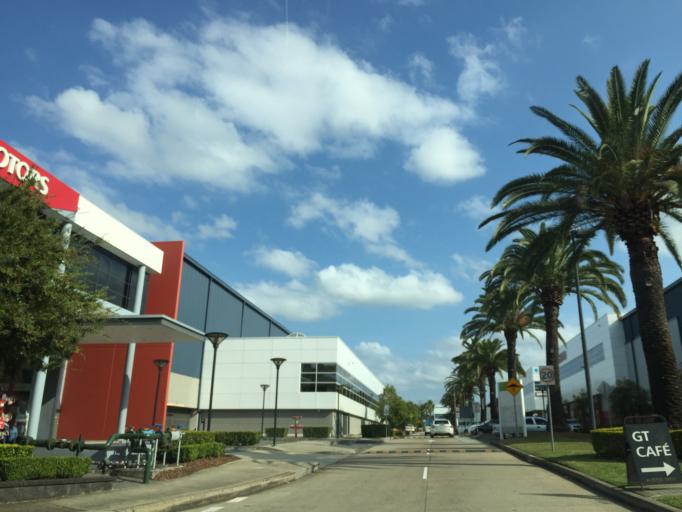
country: AU
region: New South Wales
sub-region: Strathfield
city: Homebush
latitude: -33.8569
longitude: 151.0653
